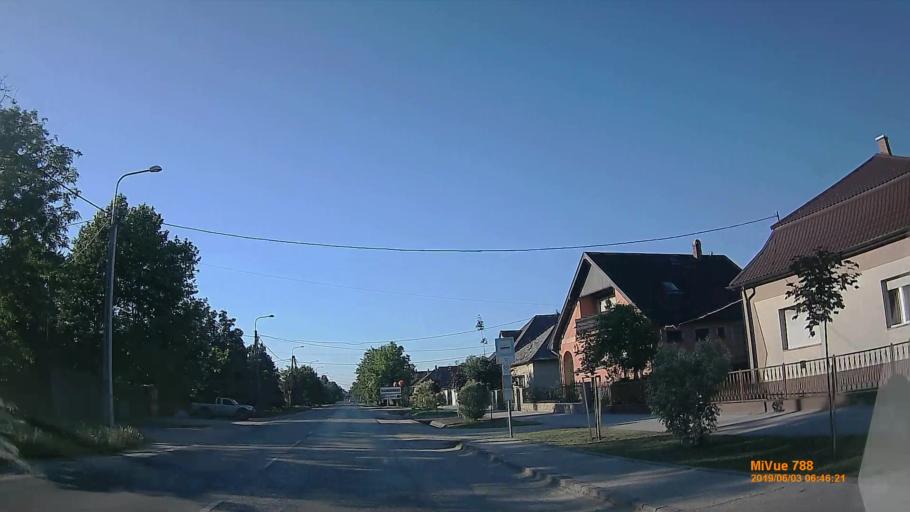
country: HU
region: Pest
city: Bugyi
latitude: 47.2318
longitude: 19.1429
